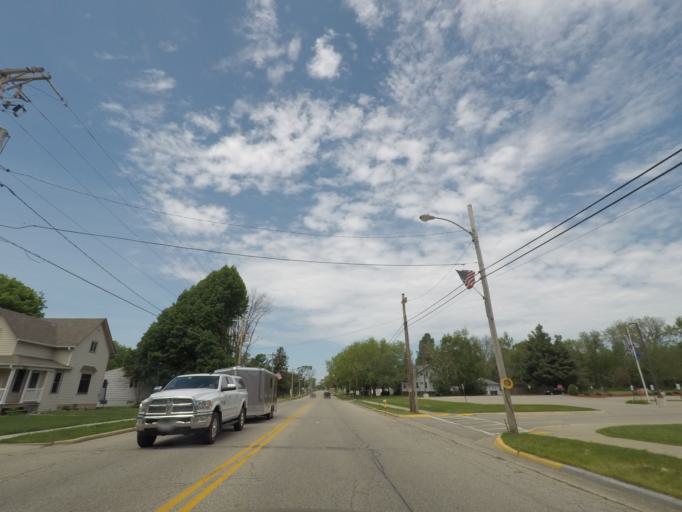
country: US
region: Wisconsin
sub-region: Rock County
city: Orfordville
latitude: 42.6308
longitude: -89.2605
